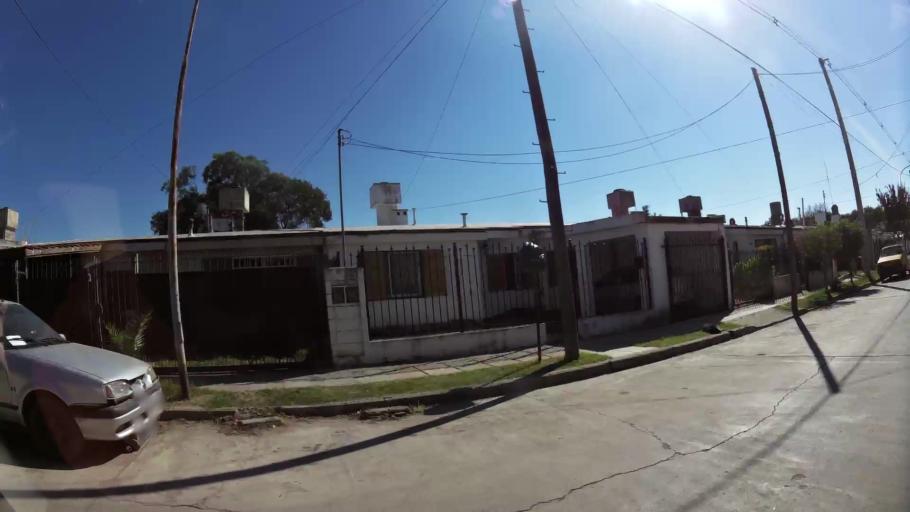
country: AR
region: Cordoba
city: Villa Allende
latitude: -31.3400
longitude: -64.2394
